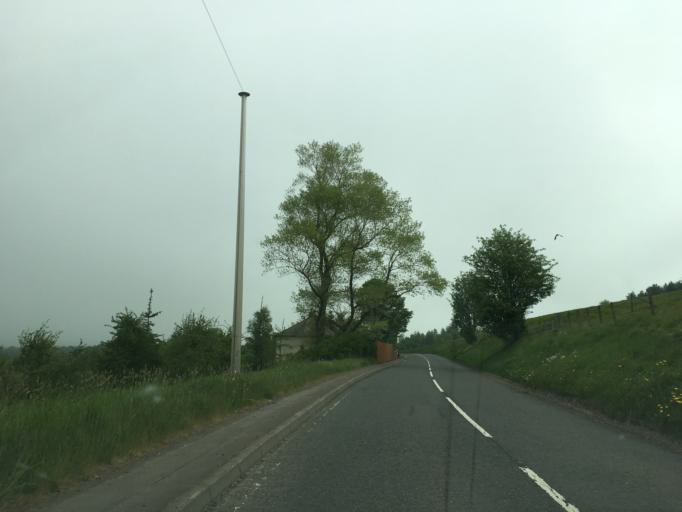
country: GB
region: Scotland
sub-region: The Scottish Borders
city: West Linton
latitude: 55.7210
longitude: -3.3341
